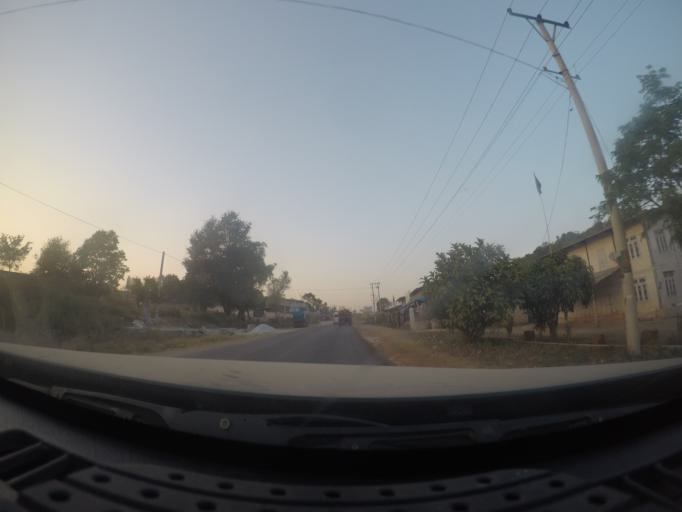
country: MM
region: Shan
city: Taunggyi
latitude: 20.6950
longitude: 97.0602
